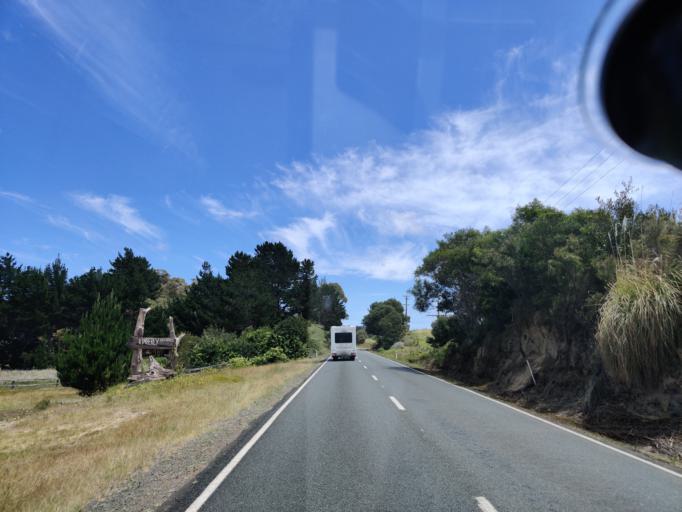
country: NZ
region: Northland
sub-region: Far North District
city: Kaitaia
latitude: -34.7492
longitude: 173.0563
